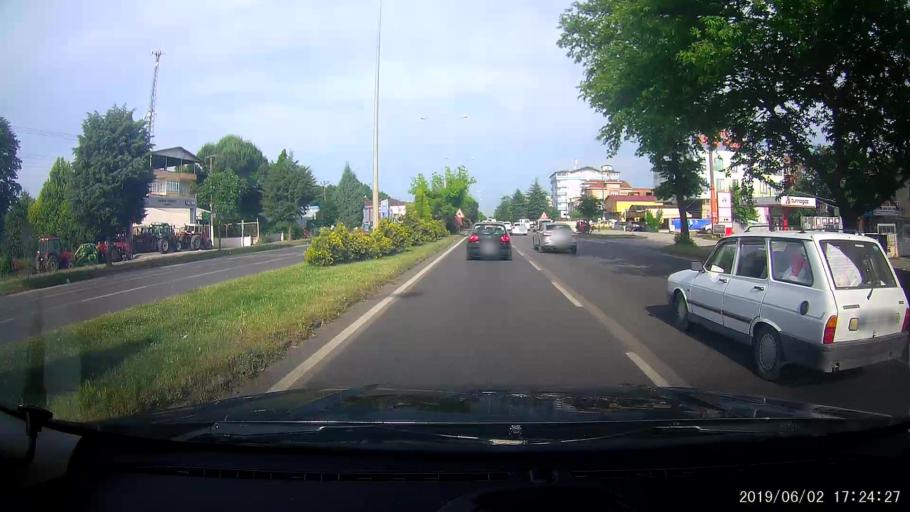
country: TR
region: Samsun
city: Carsamba
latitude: 41.2055
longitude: 36.7021
